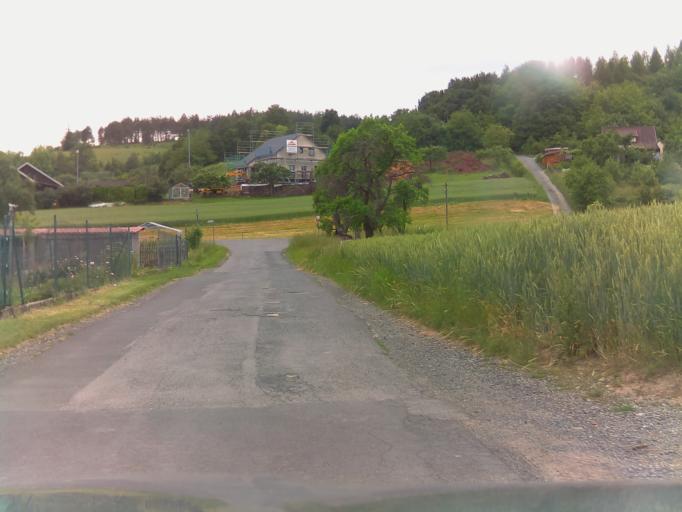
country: DE
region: Bavaria
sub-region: Regierungsbezirk Unterfranken
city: Oberelsbach
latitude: 50.4418
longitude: 10.1134
